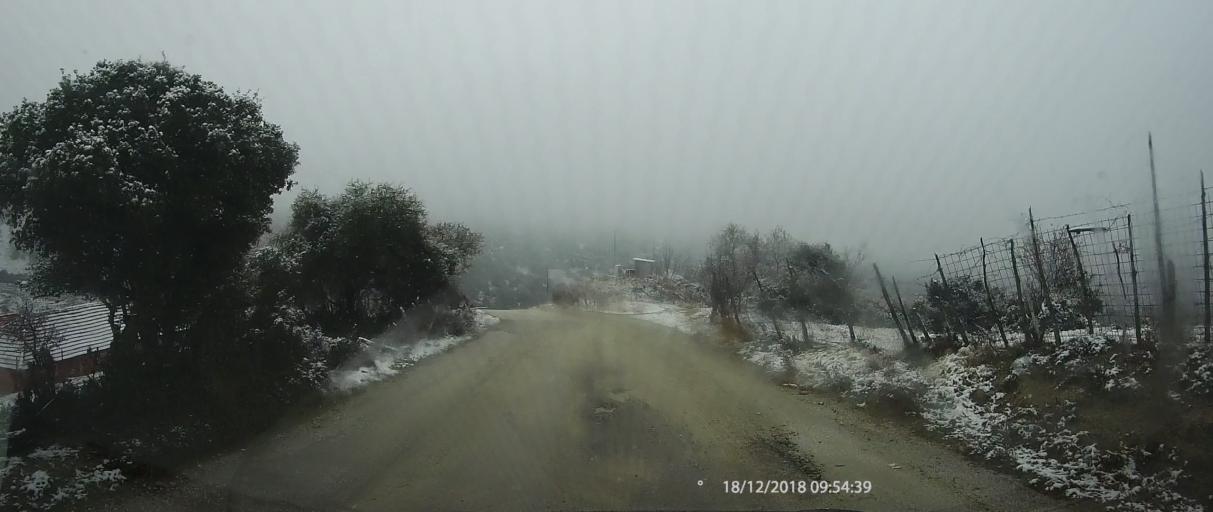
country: GR
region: Thessaly
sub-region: Nomos Larisis
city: Livadi
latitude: 40.0276
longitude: 22.2519
